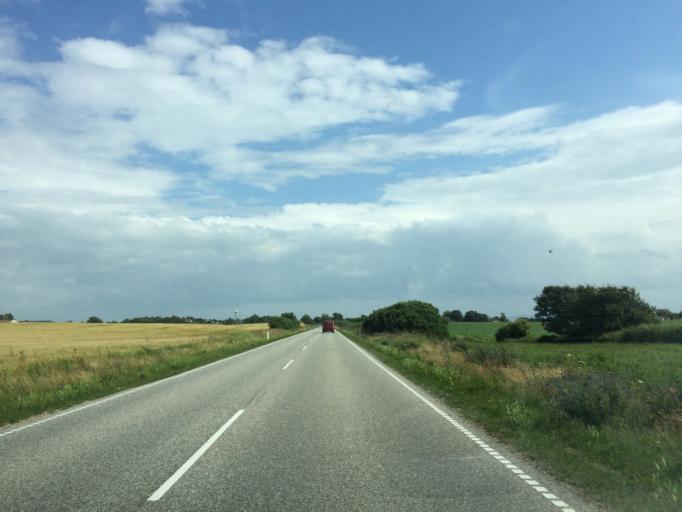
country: DK
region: Zealand
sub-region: Odsherred Kommune
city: Asnaes
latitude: 55.9690
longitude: 11.3554
